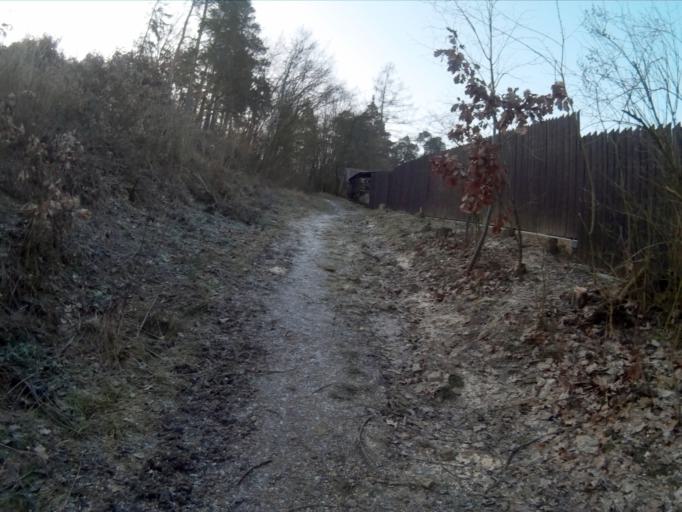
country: CZ
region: Vysocina
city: Namest' nad Oslavou
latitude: 49.2016
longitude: 16.1596
